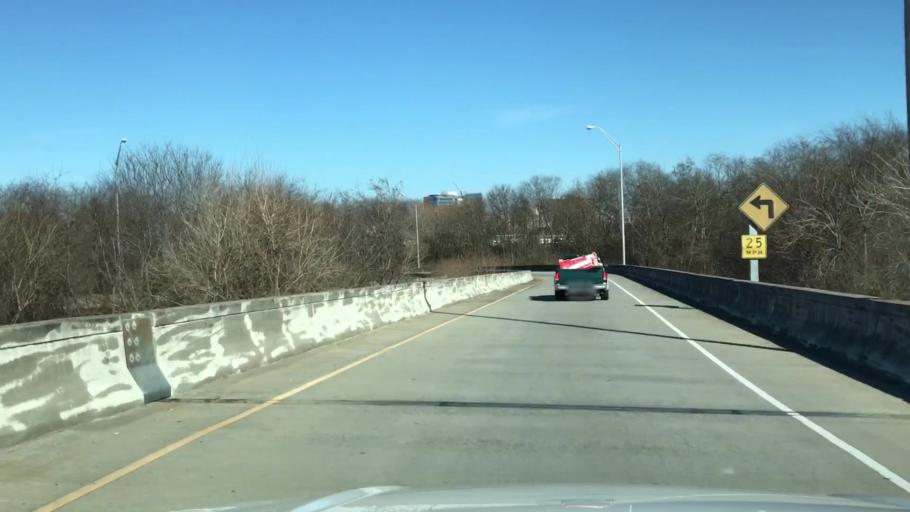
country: US
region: South Carolina
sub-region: Charleston County
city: Charleston
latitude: 32.7739
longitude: -79.9575
